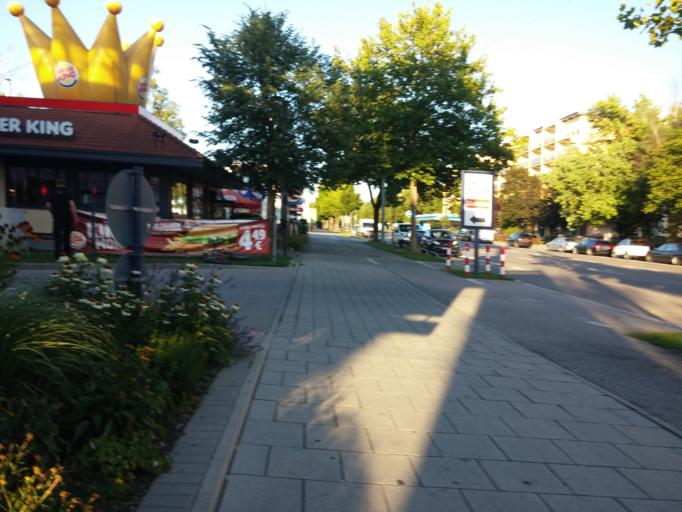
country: DE
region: Bavaria
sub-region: Upper Bavaria
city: Pasing
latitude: 48.1454
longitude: 11.4767
